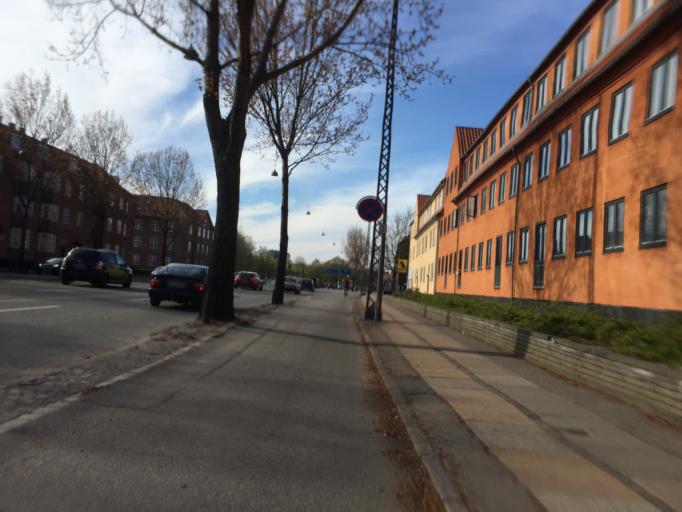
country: DK
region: Capital Region
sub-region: Frederiksberg Kommune
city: Frederiksberg
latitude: 55.7004
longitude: 12.5214
